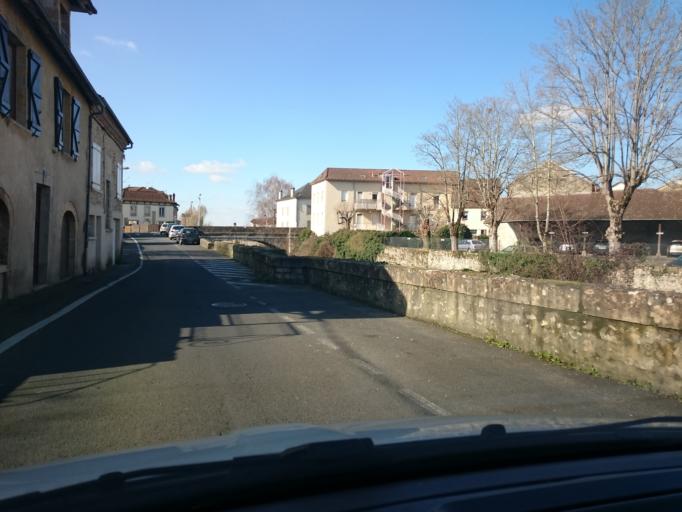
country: FR
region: Midi-Pyrenees
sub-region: Departement du Lot
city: Saint-Cere
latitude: 44.8593
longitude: 1.8882
